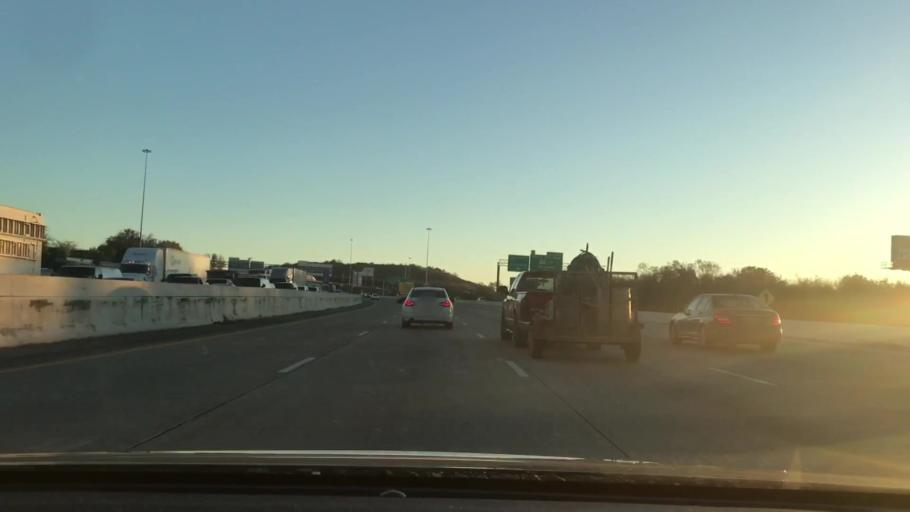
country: US
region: Tennessee
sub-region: Davidson County
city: Nashville
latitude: 36.2387
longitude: -86.7569
